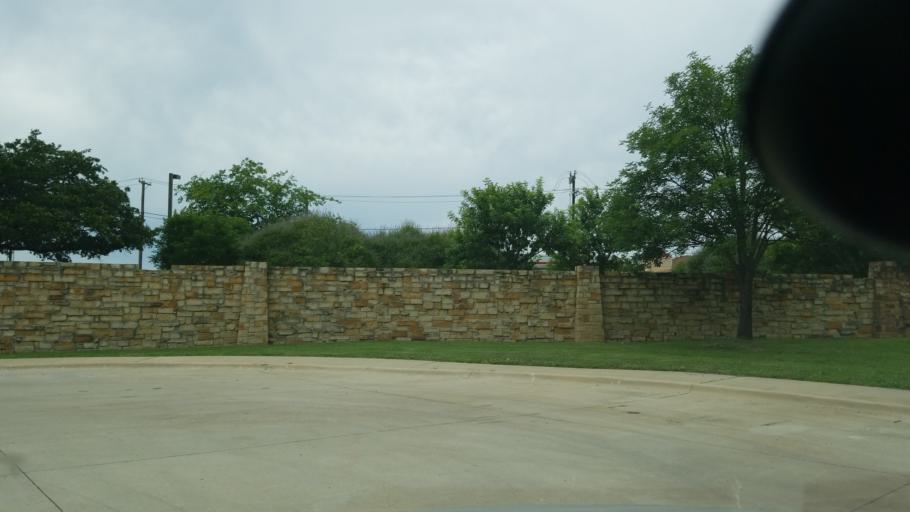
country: US
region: Texas
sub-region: Dallas County
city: Irving
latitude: 32.8388
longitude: -96.9508
